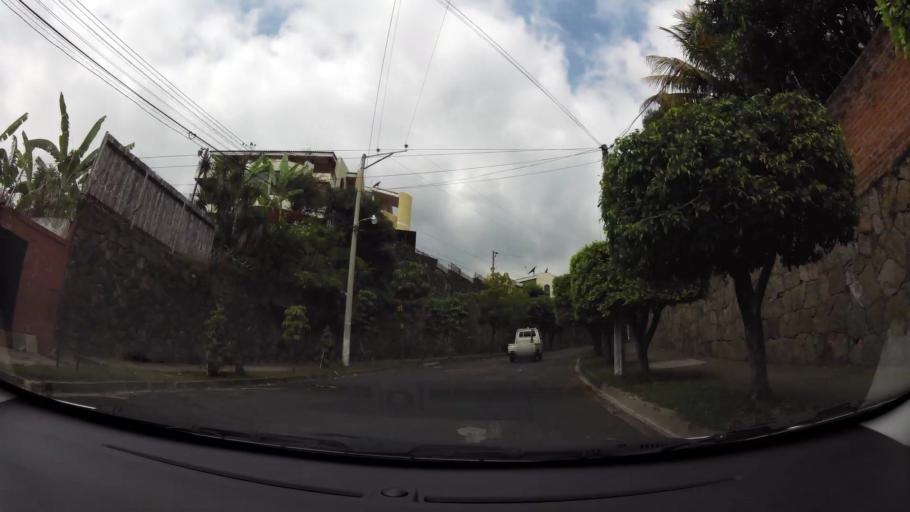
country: SV
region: La Libertad
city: Santa Tecla
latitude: 13.7090
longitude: -89.2547
